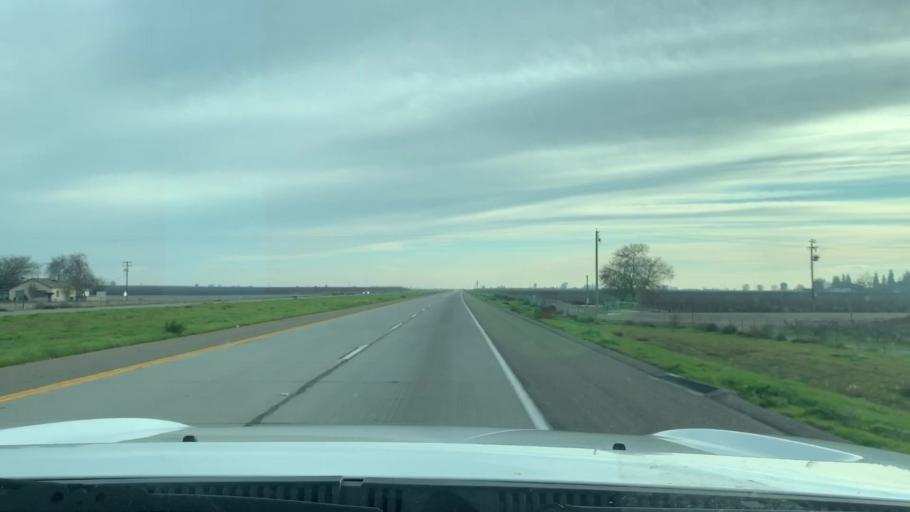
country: US
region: California
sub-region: Fresno County
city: Easton
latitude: 36.5918
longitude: -119.7862
